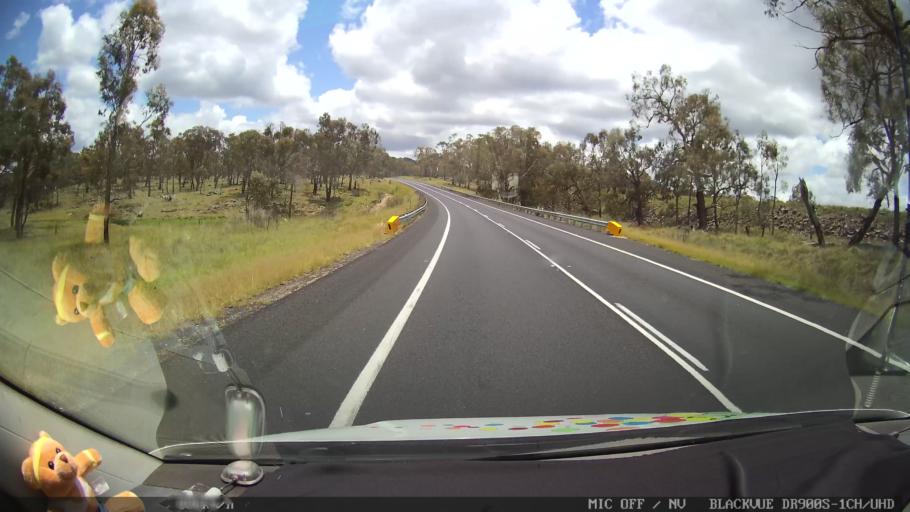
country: AU
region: New South Wales
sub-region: Glen Innes Severn
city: Glen Innes
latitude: -29.3679
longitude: 151.8976
